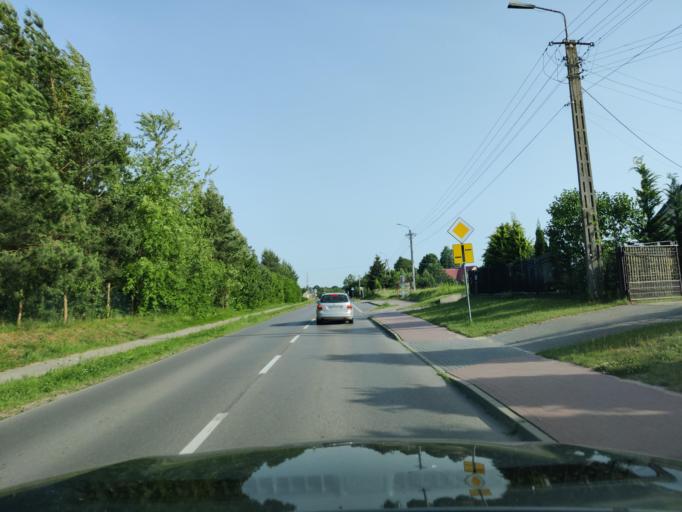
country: PL
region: Masovian Voivodeship
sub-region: Powiat wyszkowski
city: Wyszkow
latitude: 52.6475
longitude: 21.4503
